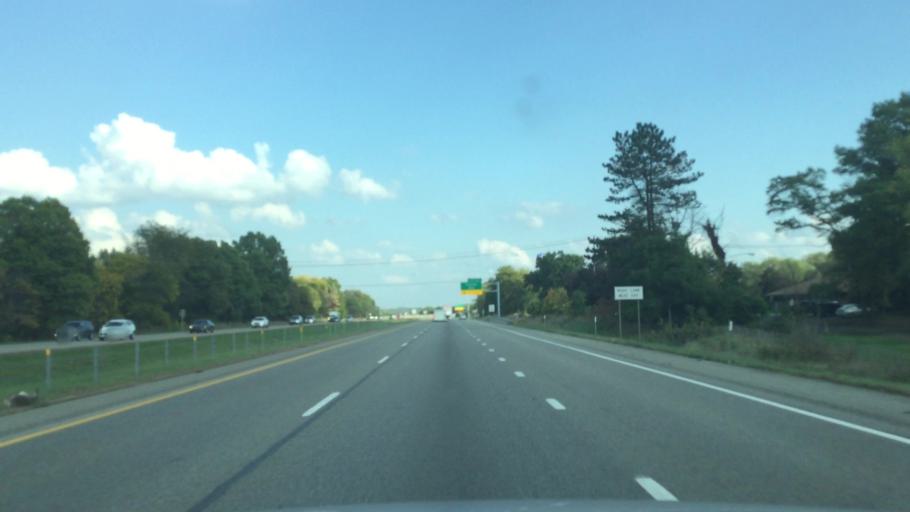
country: US
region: Michigan
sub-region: Calhoun County
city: Lakeview
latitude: 42.2630
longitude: -85.2093
